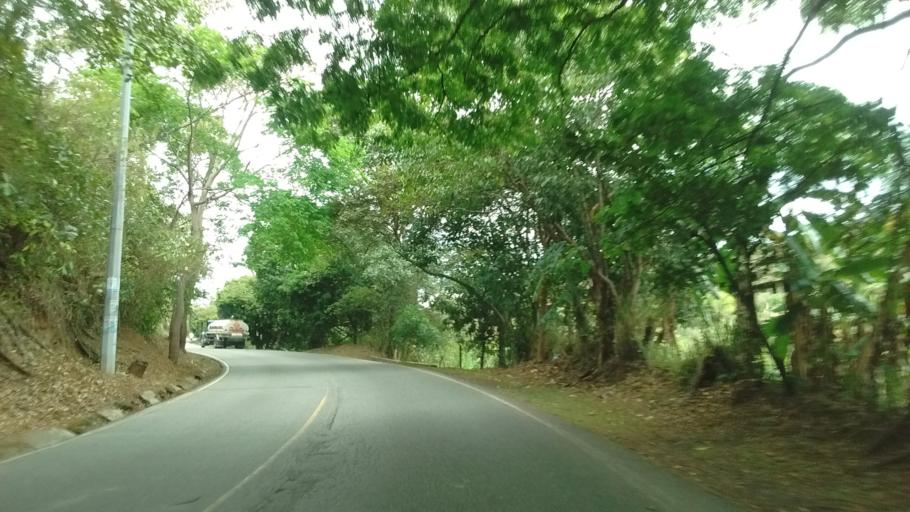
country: CO
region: Cauca
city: La Sierra
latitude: 2.1905
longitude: -76.8392
